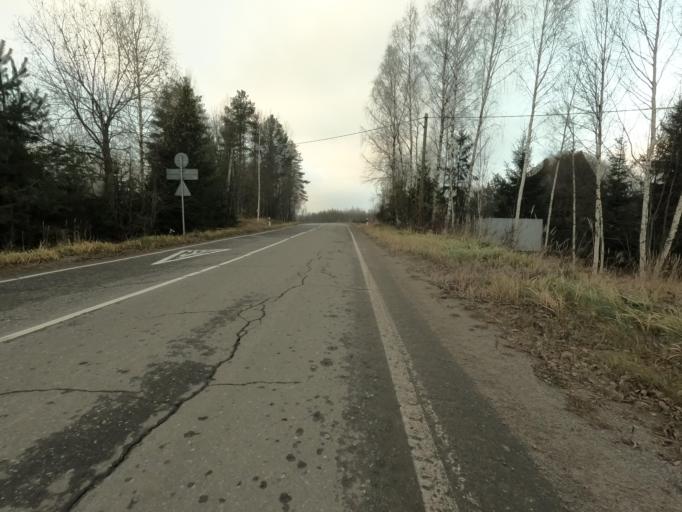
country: RU
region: Leningrad
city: Kirovsk
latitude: 59.8020
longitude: 30.9876
